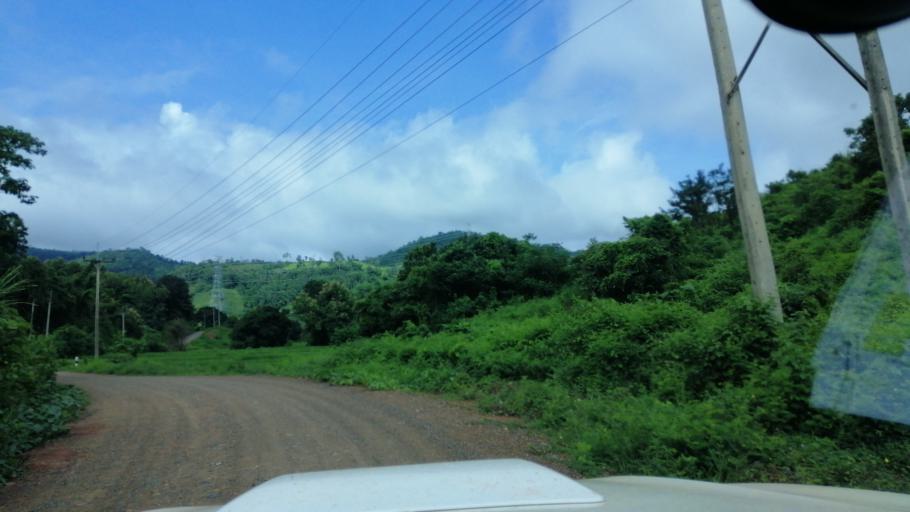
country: LA
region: Xiagnabouli
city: Muang Kenthao
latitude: 17.9136
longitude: 101.3550
